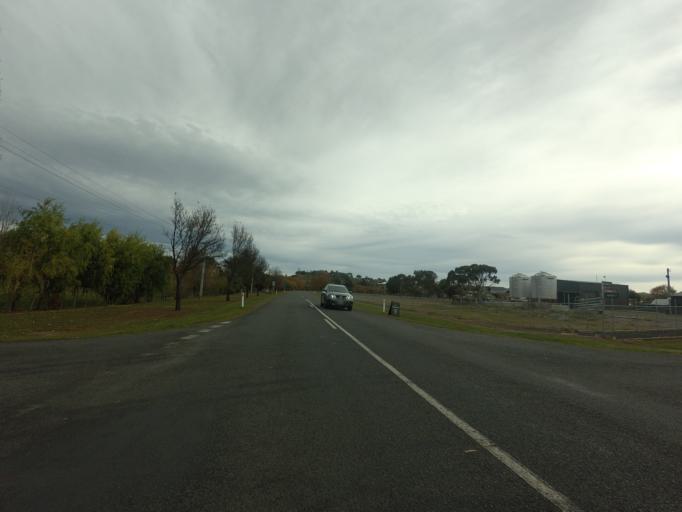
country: AU
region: Tasmania
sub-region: Derwent Valley
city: New Norfolk
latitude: -42.3838
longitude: 147.0054
